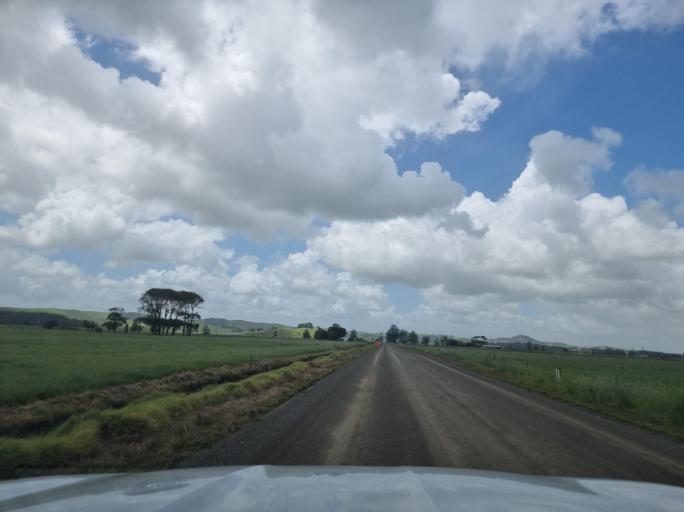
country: NZ
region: Northland
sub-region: Kaipara District
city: Dargaville
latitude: -36.0866
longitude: 174.0323
